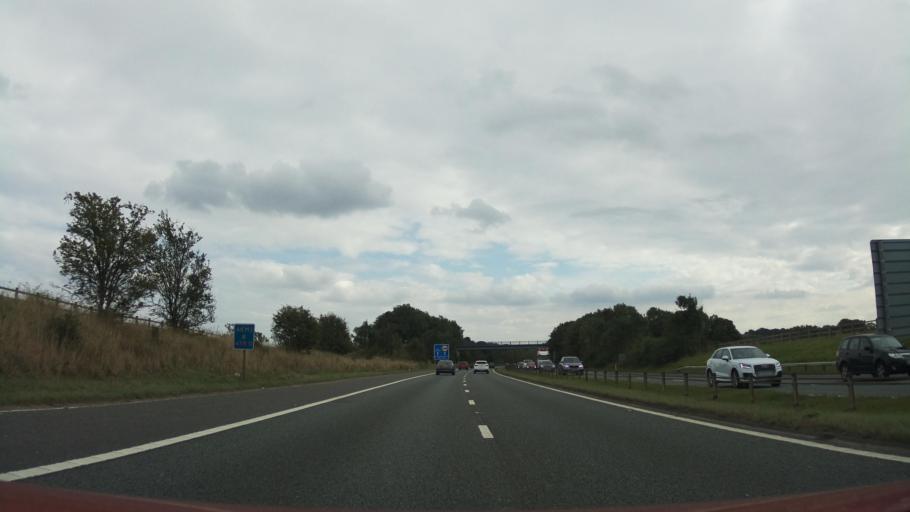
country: GB
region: England
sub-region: County Durham
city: Chester-le-Street
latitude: 54.8541
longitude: -1.5409
